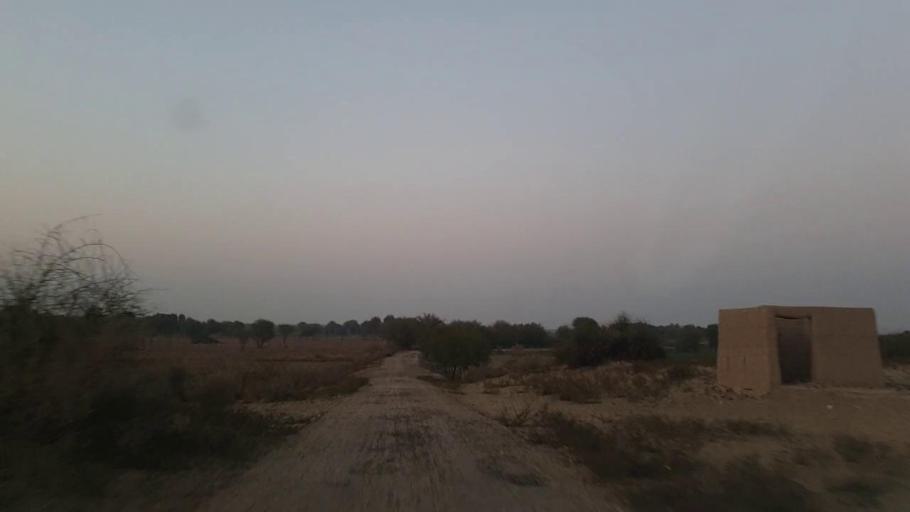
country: PK
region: Sindh
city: Bandhi
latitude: 26.6255
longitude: 68.3954
